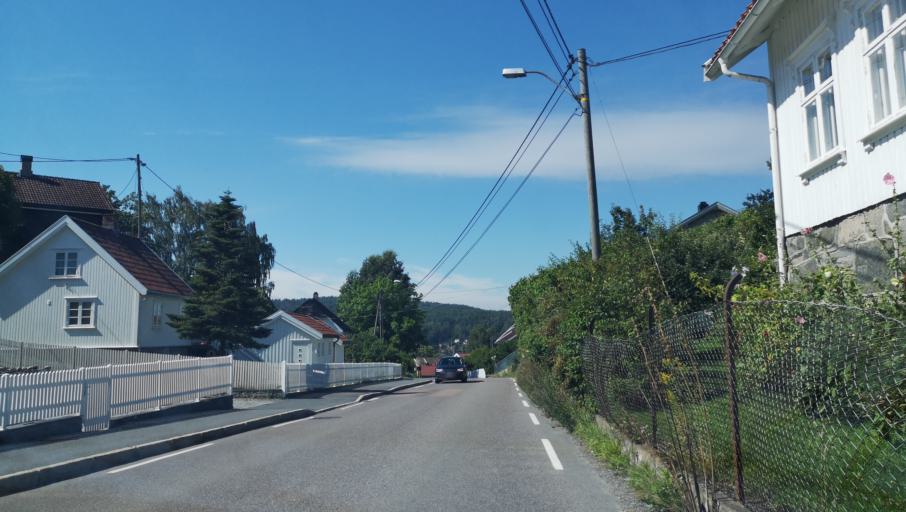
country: NO
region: Ostfold
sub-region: Moss
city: Moss
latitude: 59.5226
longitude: 10.6933
